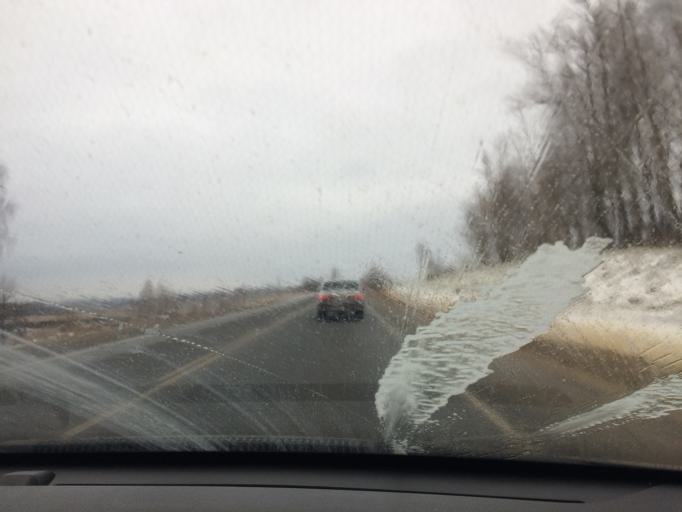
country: RU
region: Tula
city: Gorelki
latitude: 54.2442
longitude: 37.6660
